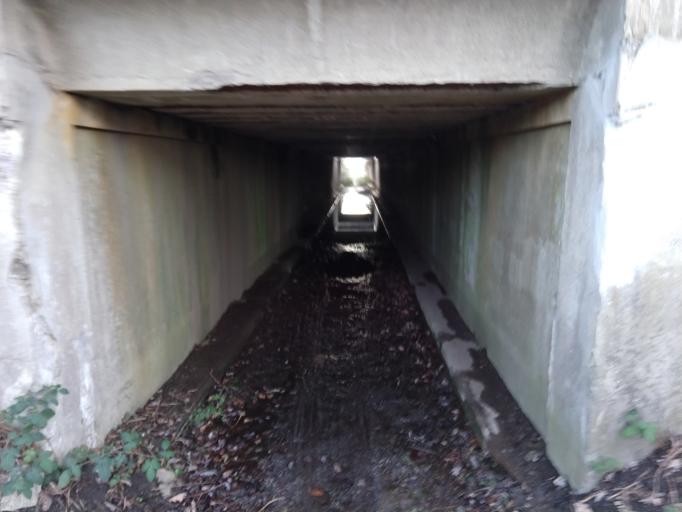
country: DE
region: North Rhine-Westphalia
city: Oelde
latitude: 51.8257
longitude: 8.1213
